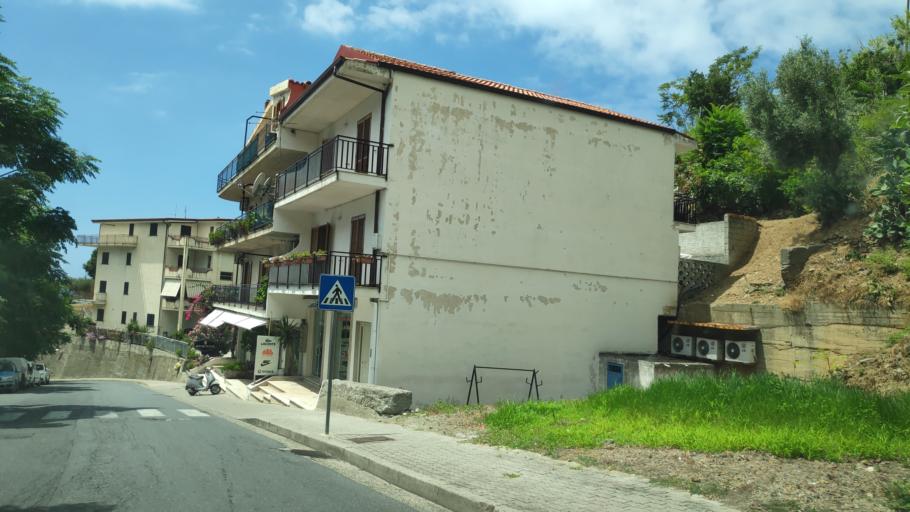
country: IT
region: Calabria
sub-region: Provincia di Cosenza
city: Paola
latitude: 39.3610
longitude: 16.0355
